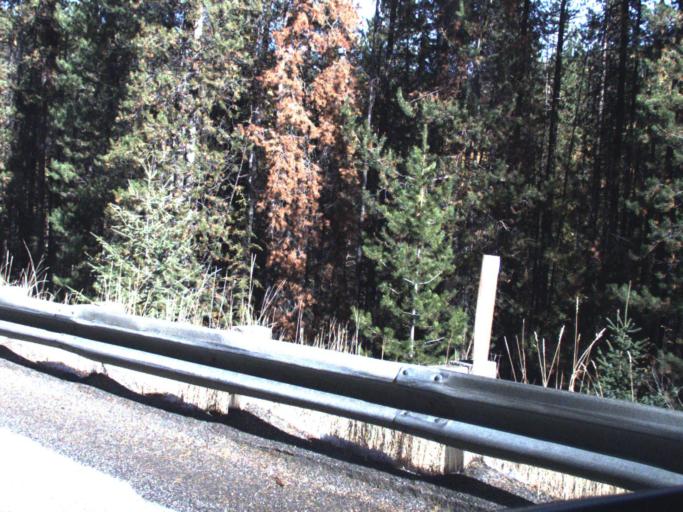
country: US
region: Washington
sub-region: Ferry County
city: Republic
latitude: 48.6270
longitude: -118.4433
